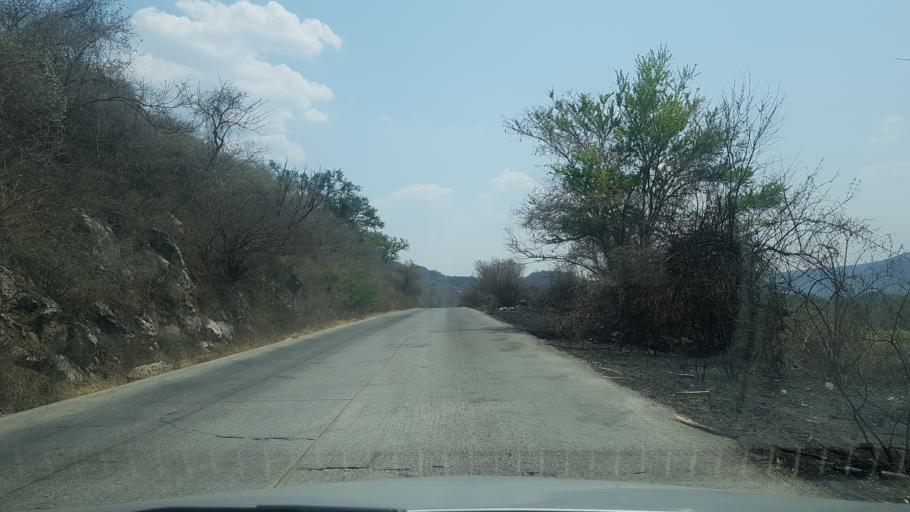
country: MX
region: Morelos
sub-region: Tlaltizapan de Zapata
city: Colonia Palo Prieto (Chipitongo)
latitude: 18.7660
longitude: -99.1075
